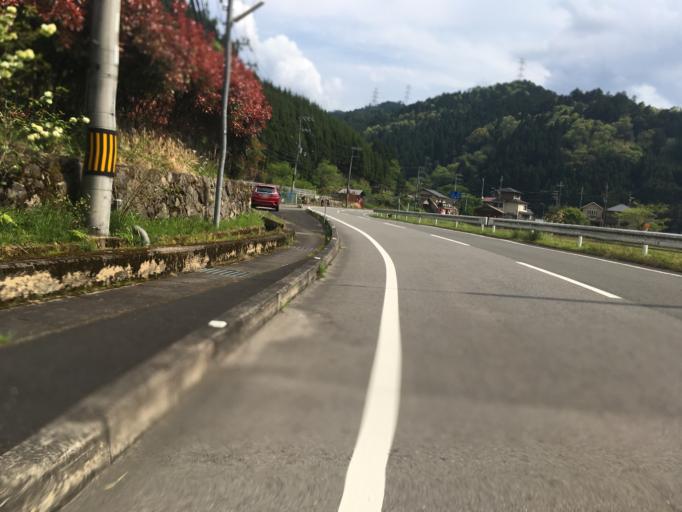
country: JP
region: Kyoto
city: Kameoka
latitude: 35.1421
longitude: 135.5909
